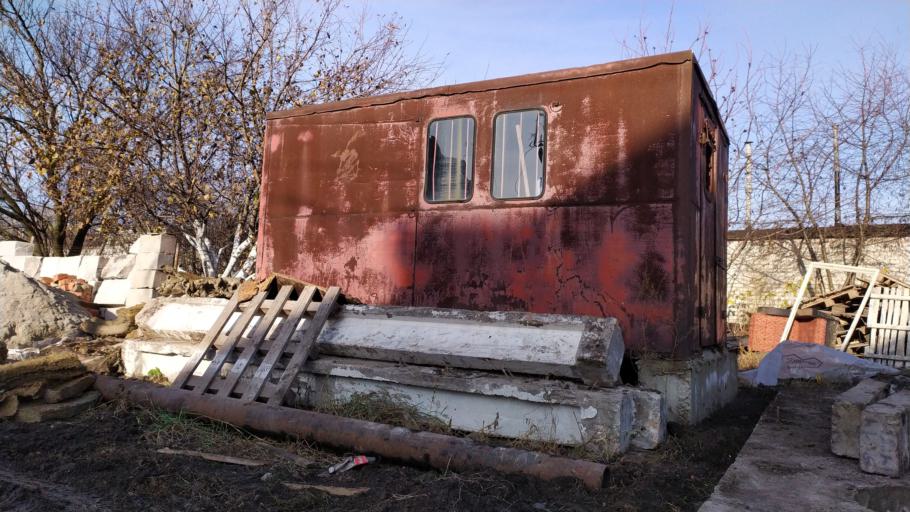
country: RU
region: Kursk
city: Kursk
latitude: 51.6446
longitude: 36.1339
